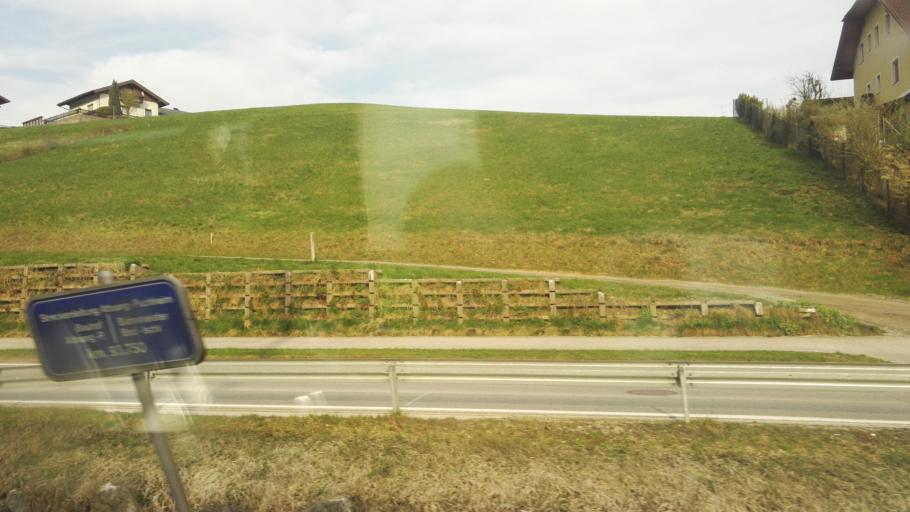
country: AT
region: Upper Austria
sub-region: Politischer Bezirk Gmunden
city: Altmunster
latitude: 47.9151
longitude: 13.7688
